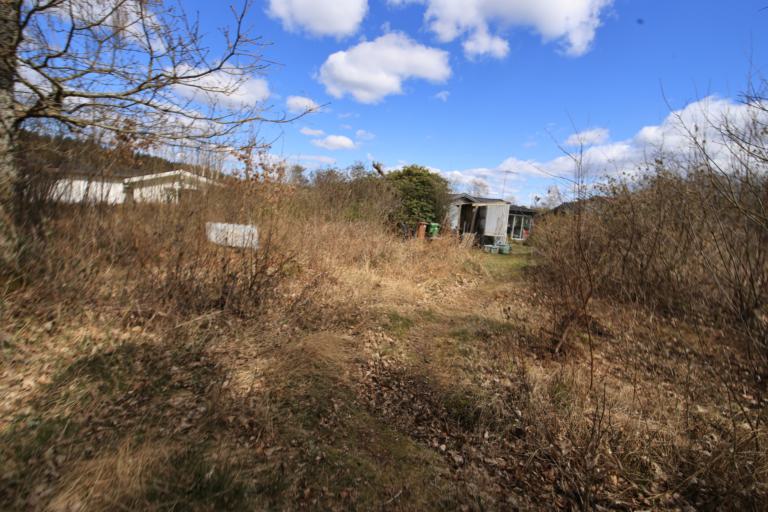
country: SE
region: Halland
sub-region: Varbergs Kommun
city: Varberg
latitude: 57.1828
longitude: 12.2356
